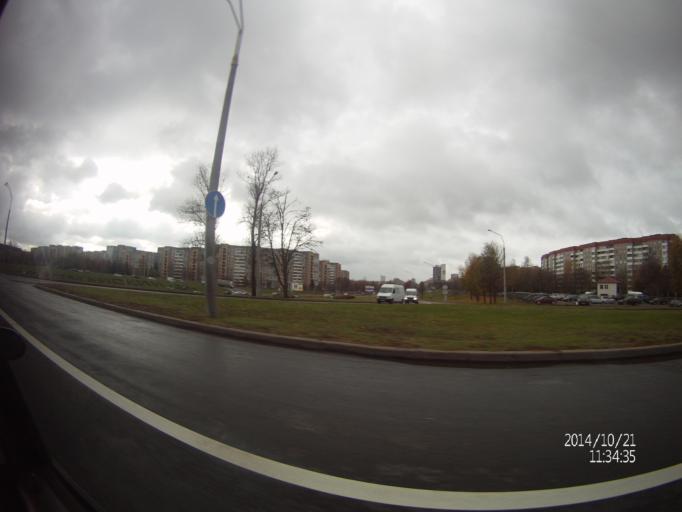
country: BY
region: Minsk
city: Borovlyany
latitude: 53.9604
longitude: 27.6253
